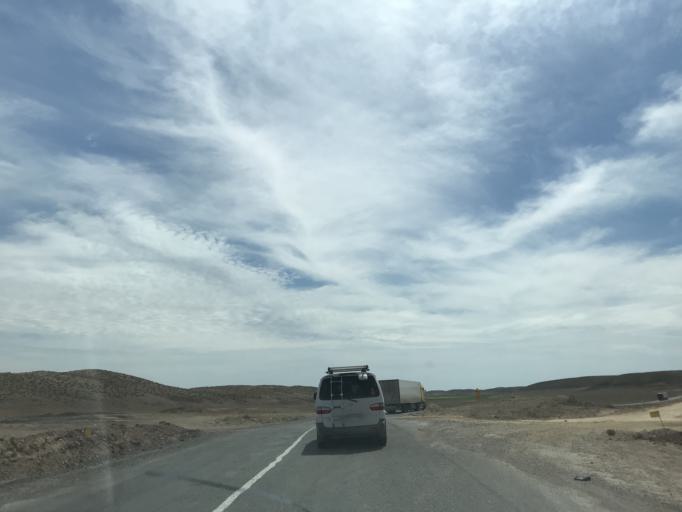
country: KZ
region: Almaty Oblysy
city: Ulken
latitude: 45.0681
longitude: 73.9950
